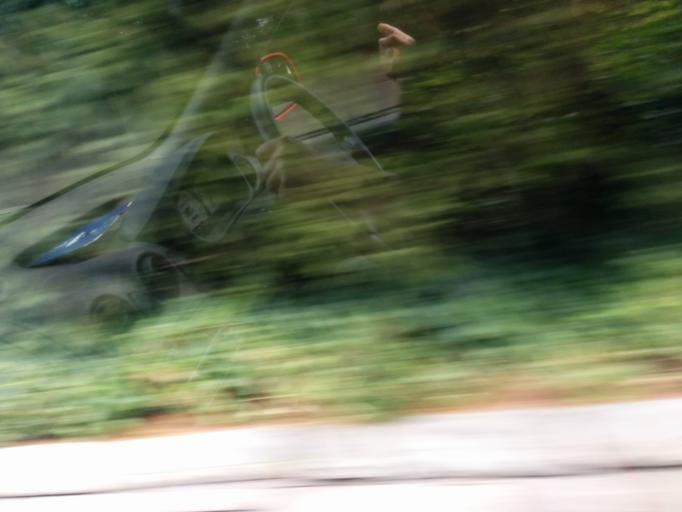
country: CH
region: Zurich
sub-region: Bezirk Meilen
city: Kuesnacht / Heslibach
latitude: 47.3149
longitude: 8.5890
